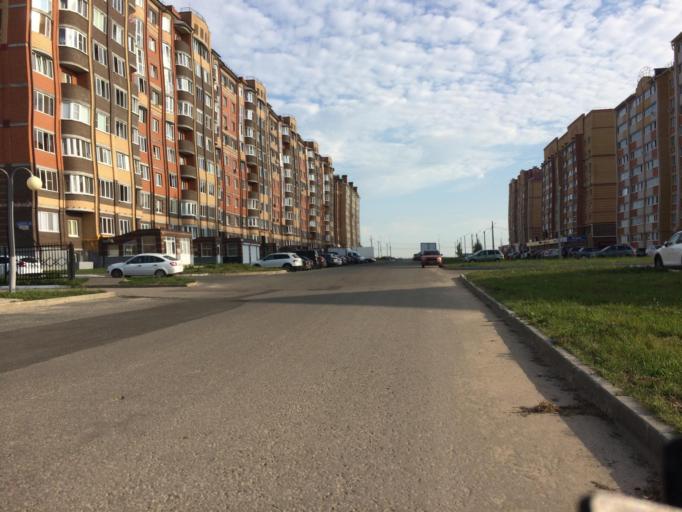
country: RU
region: Mariy-El
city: Medvedevo
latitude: 56.6365
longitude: 47.8123
